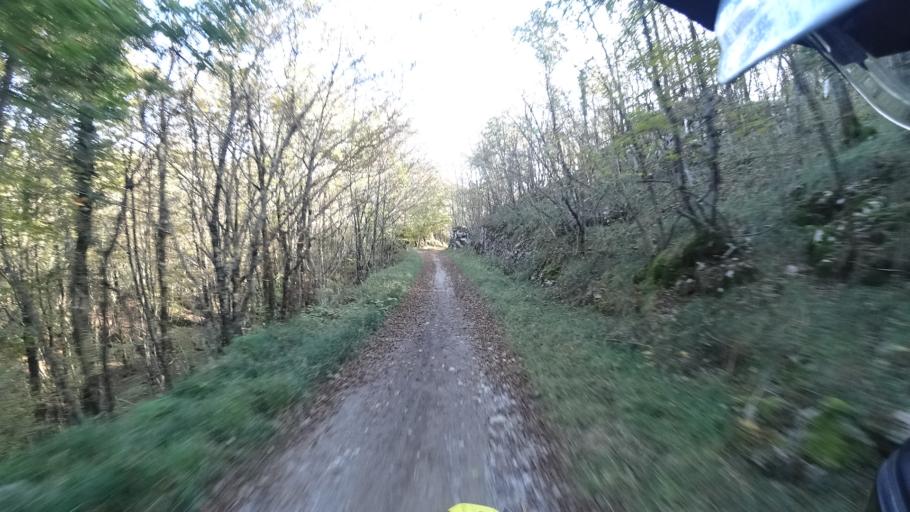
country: HR
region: Primorsko-Goranska
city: Kastav
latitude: 45.4025
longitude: 14.3287
